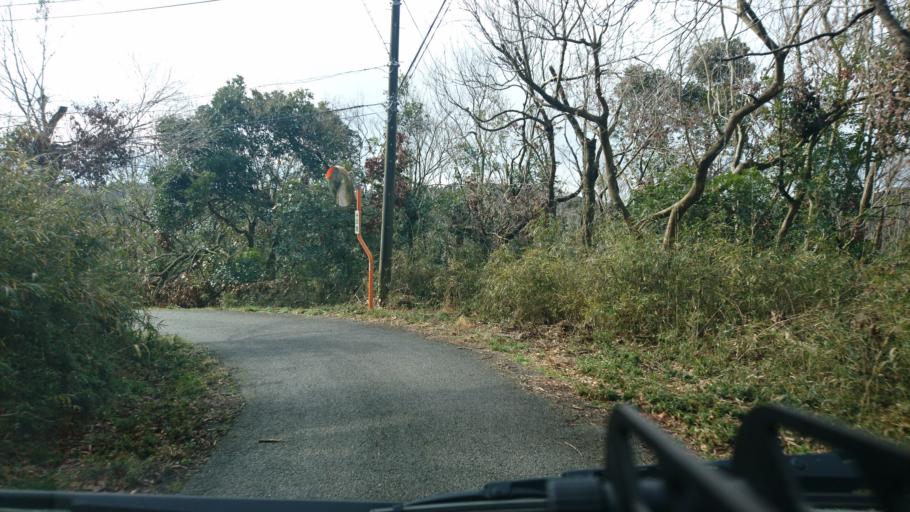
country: JP
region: Chiba
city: Kisarazu
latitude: 35.3264
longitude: 139.9661
